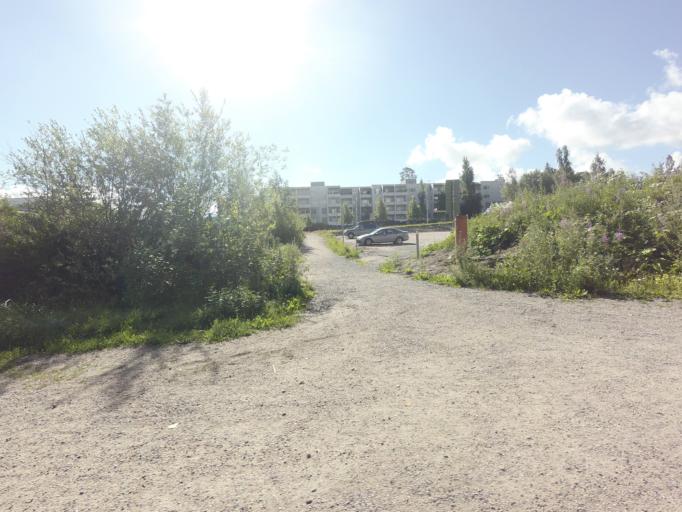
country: FI
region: Uusimaa
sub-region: Helsinki
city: Espoo
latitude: 60.1522
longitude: 24.6503
